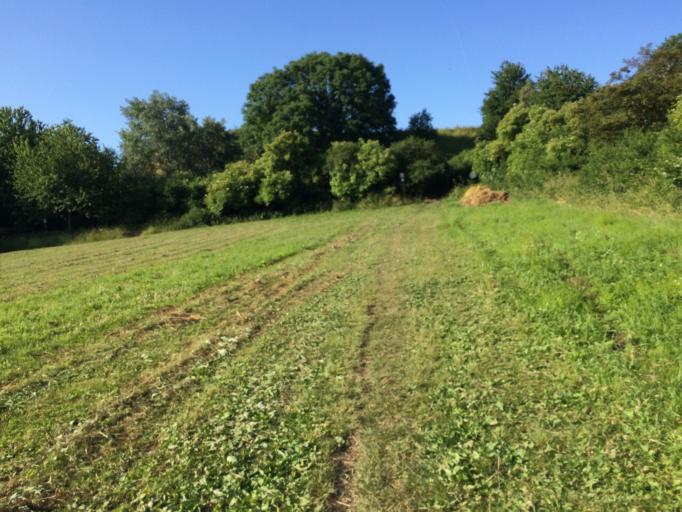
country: CZ
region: Central Bohemia
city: Horomerice
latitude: 50.0975
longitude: 14.3217
